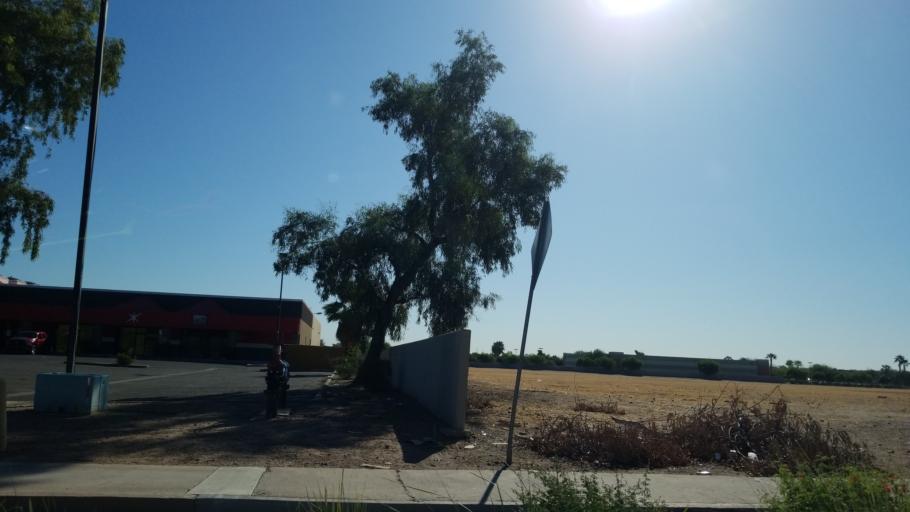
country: US
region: Arizona
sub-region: Maricopa County
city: Avondale
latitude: 33.4481
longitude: -112.3496
